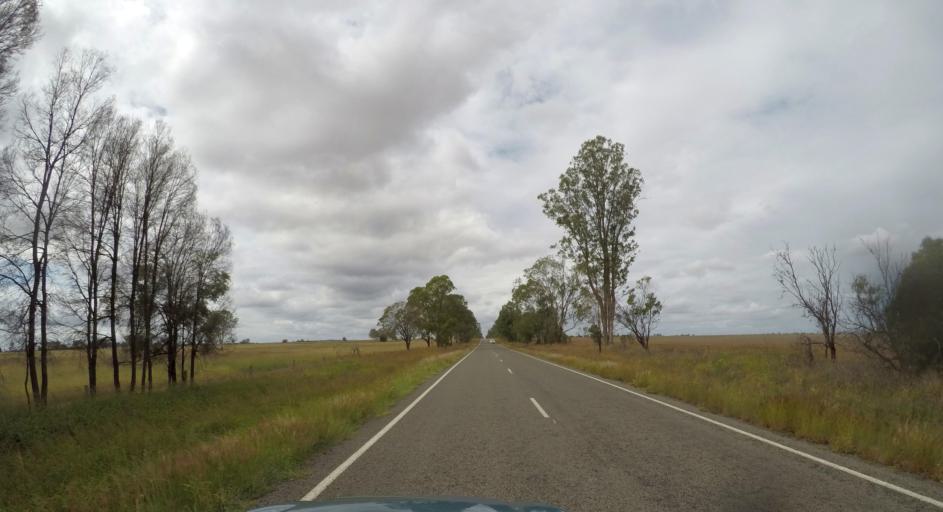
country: AU
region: Queensland
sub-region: South Burnett
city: Kingaroy
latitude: -26.3927
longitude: 151.2235
